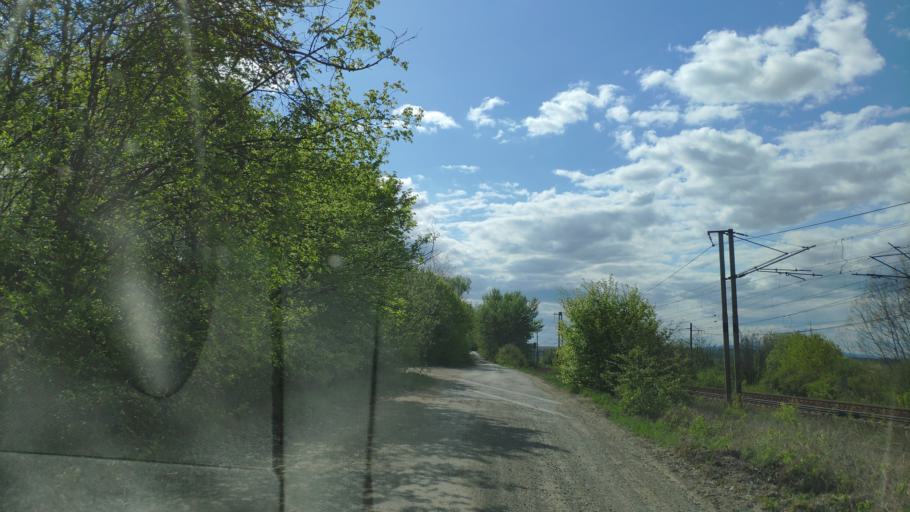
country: SK
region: Kosicky
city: Kosice
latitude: 48.6768
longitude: 21.4445
